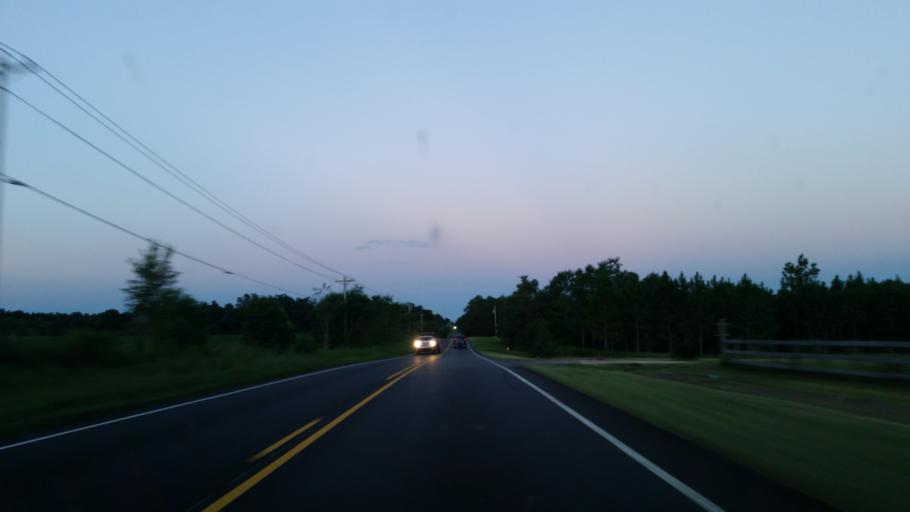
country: US
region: Alabama
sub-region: Baldwin County
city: Robertsdale
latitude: 30.5676
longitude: -87.6362
